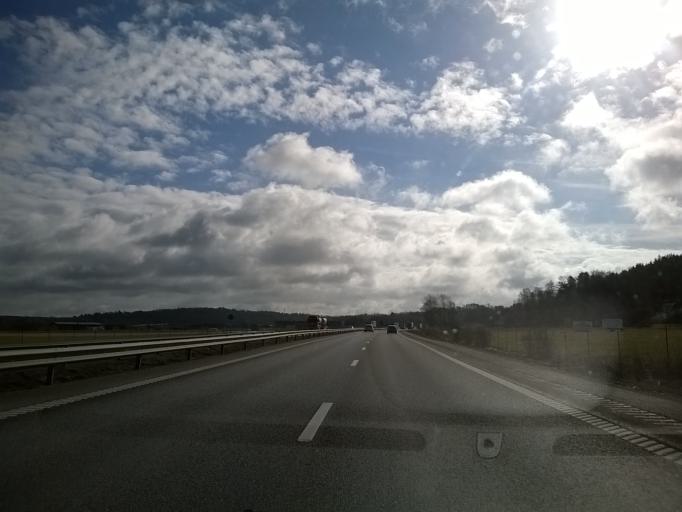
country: SE
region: Halland
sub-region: Kungsbacka Kommun
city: Fjaeras kyrkby
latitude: 57.4352
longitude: 12.1432
